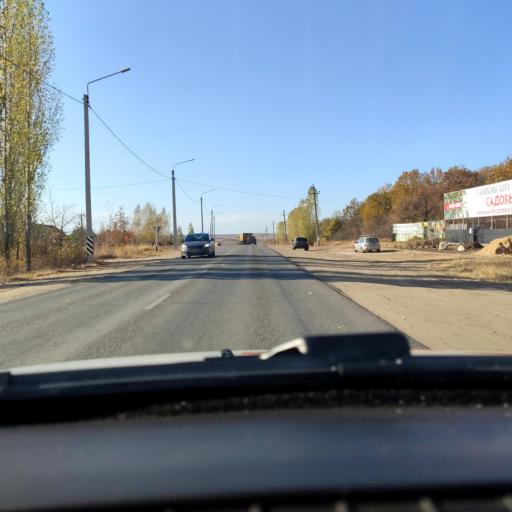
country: RU
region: Voronezj
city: Semiluki
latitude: 51.7265
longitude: 39.0327
